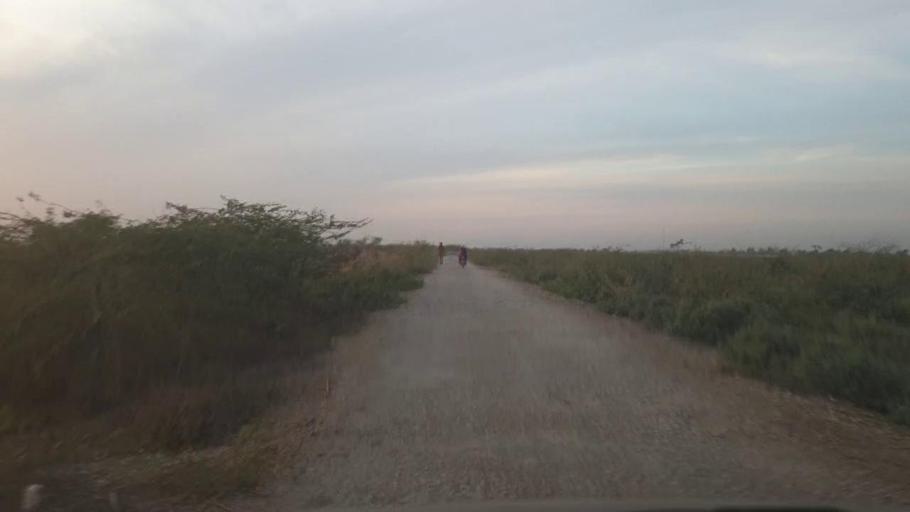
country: PK
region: Sindh
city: Kunri
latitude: 25.2303
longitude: 69.5322
